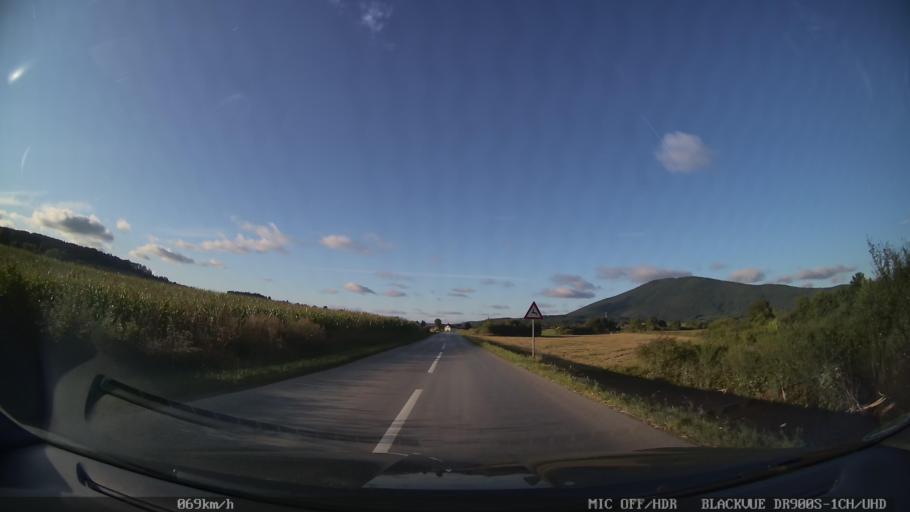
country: HR
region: Karlovacka
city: Plaski
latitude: 45.1038
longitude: 15.3591
